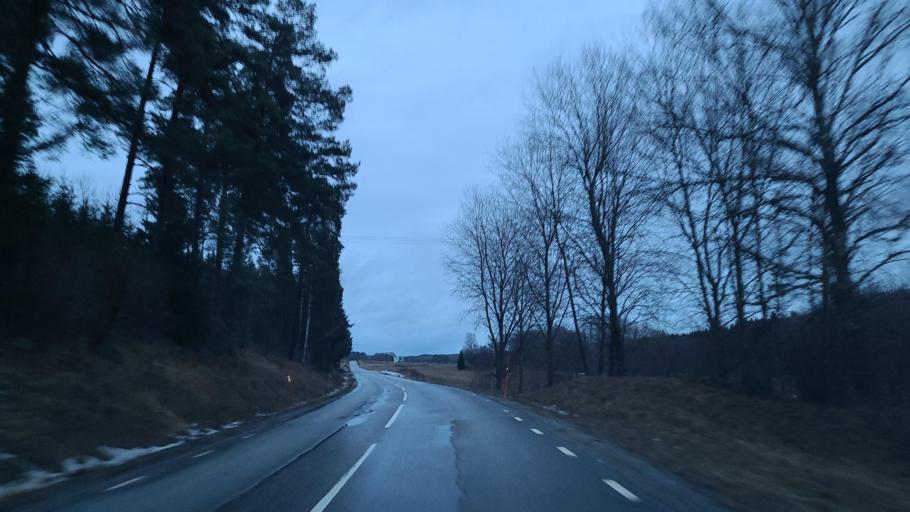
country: SE
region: Stockholm
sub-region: Norrtalje Kommun
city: Norrtalje
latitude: 59.7354
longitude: 18.6192
